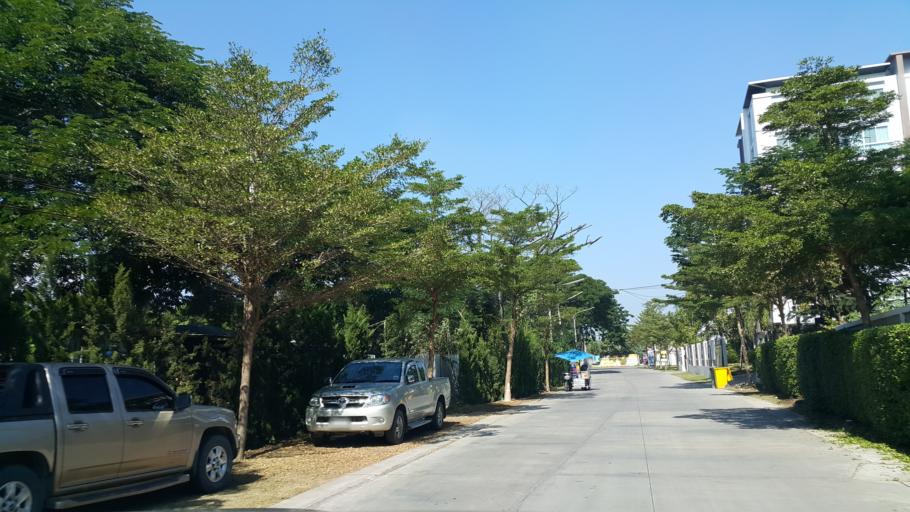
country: TH
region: Chiang Mai
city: Chiang Mai
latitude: 18.7671
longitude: 98.9907
